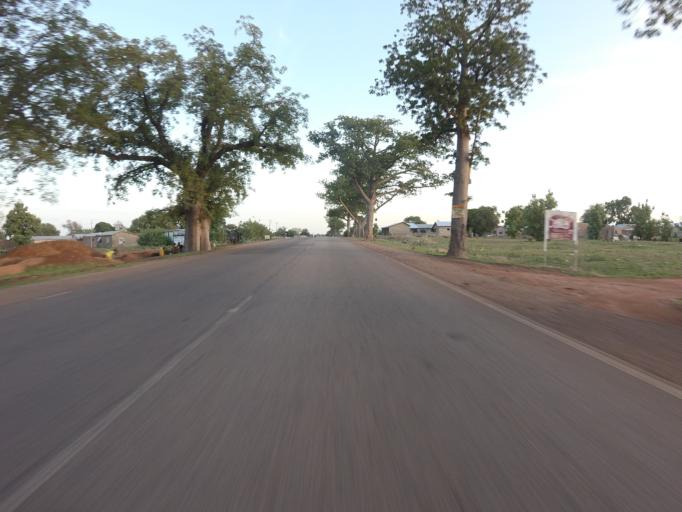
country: GH
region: Upper East
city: Navrongo
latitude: 10.9216
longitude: -1.0894
